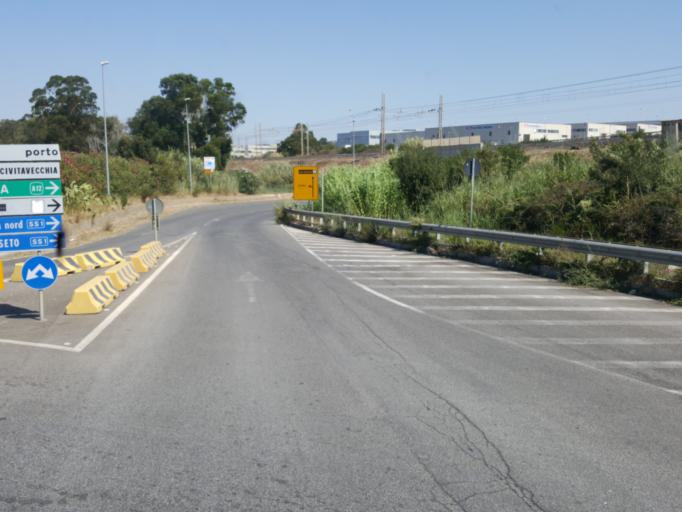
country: IT
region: Latium
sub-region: Citta metropolitana di Roma Capitale
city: Aurelia
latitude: 42.1182
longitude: 11.7702
